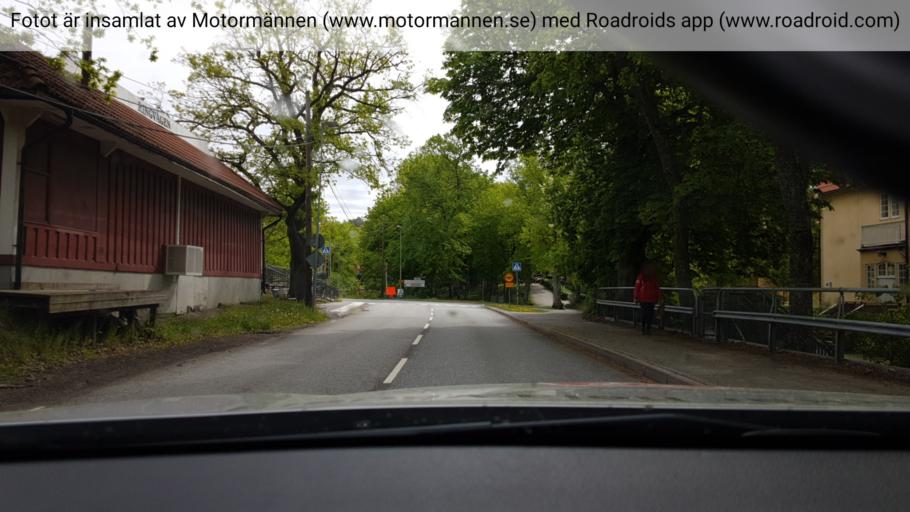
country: SE
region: Stockholm
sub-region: Nacka Kommun
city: Saltsjobaden
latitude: 59.2832
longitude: 18.3018
